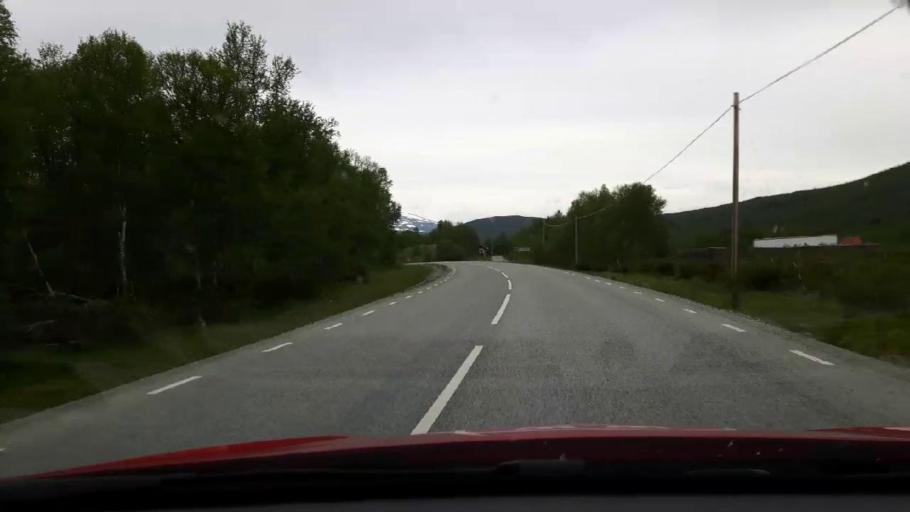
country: NO
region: Sor-Trondelag
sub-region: Tydal
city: Aas
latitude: 62.6933
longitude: 12.4071
